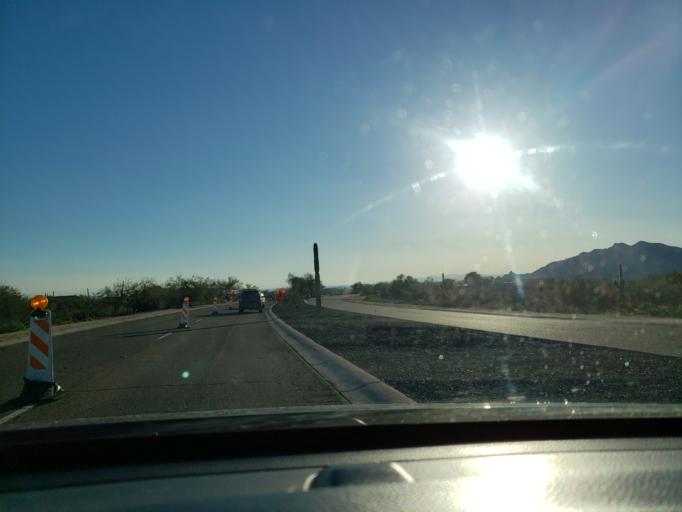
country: US
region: Arizona
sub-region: Maricopa County
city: Carefree
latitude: 33.8206
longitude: -111.8845
